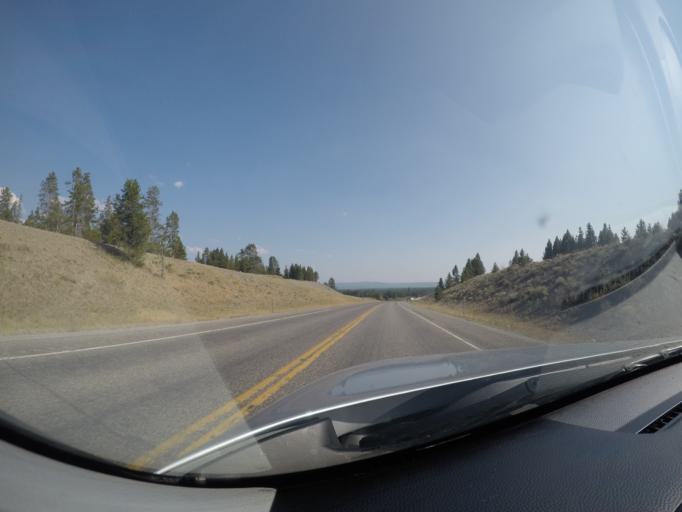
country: US
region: Montana
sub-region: Gallatin County
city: West Yellowstone
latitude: 44.7210
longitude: -111.1038
